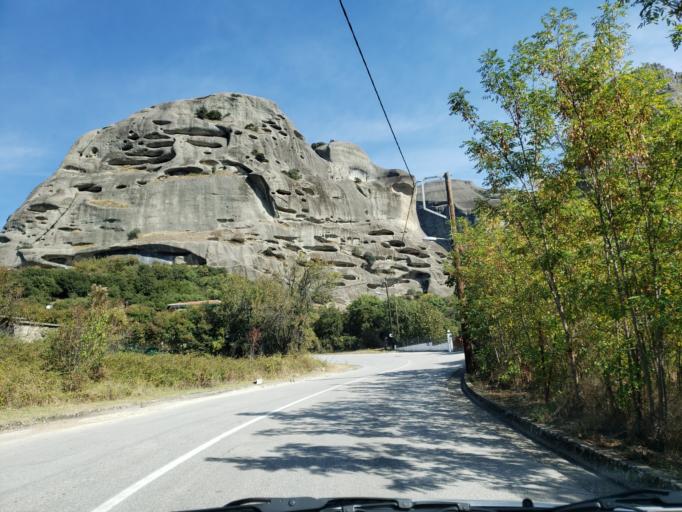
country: GR
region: Thessaly
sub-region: Trikala
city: Kastraki
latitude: 39.7084
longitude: 21.6180
